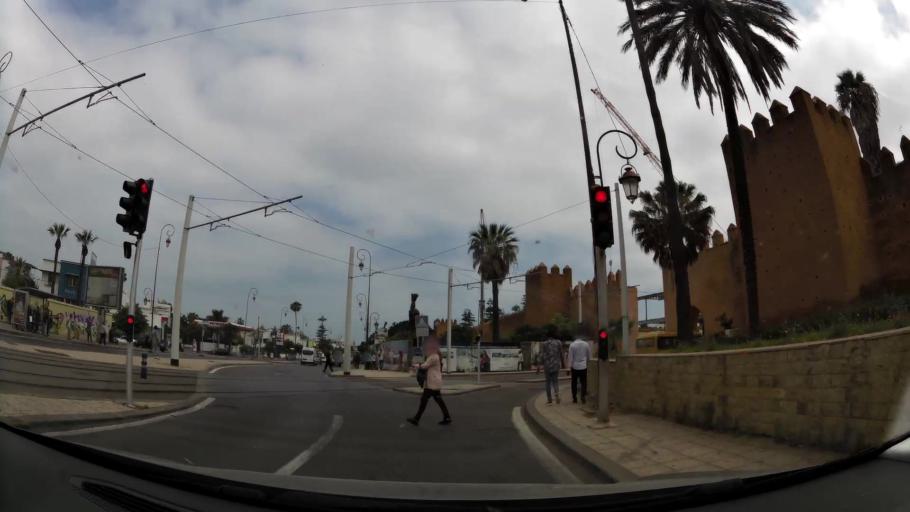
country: MA
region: Rabat-Sale-Zemmour-Zaer
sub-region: Rabat
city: Rabat
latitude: 34.0148
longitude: -6.8385
